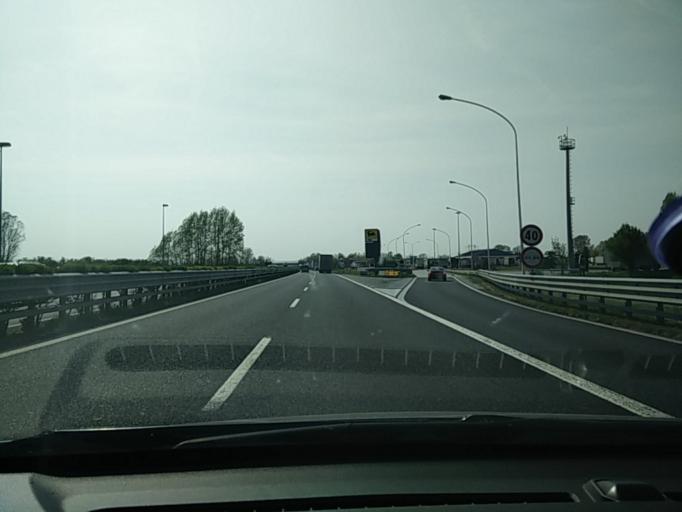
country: IT
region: Veneto
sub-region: Provincia di Venezia
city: Teglio Veneto
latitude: 45.8048
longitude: 12.8857
